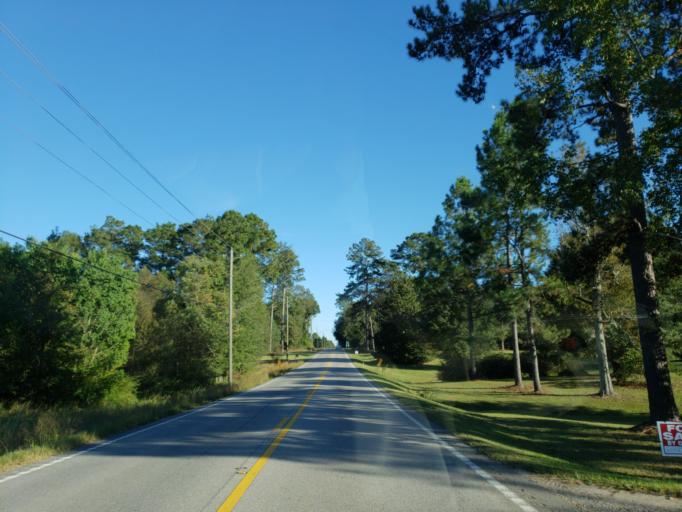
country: US
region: Mississippi
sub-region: Perry County
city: Richton
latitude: 31.3560
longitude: -88.9574
